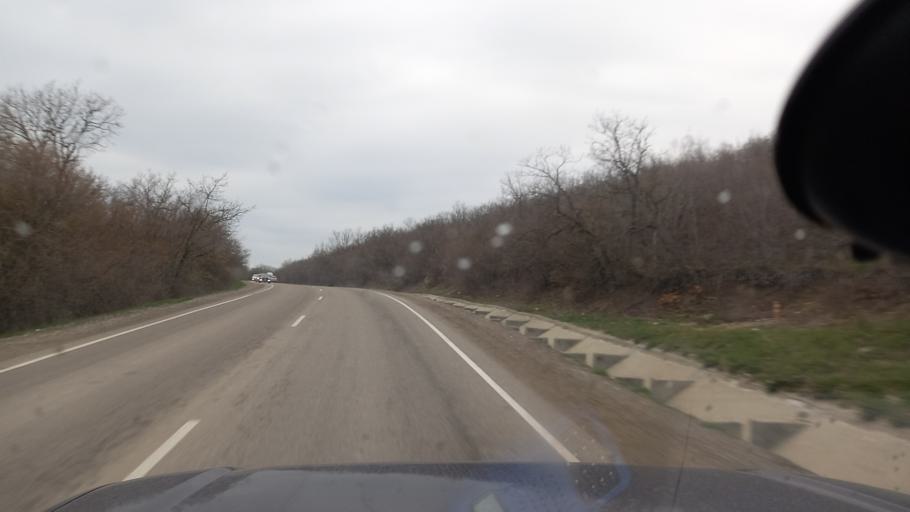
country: RU
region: Krasnodarskiy
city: Sukko
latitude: 44.8410
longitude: 37.4146
